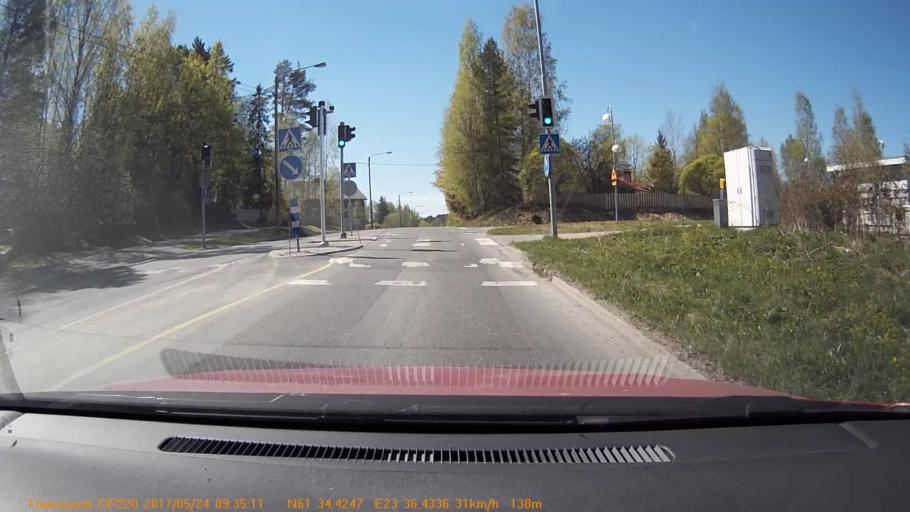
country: FI
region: Pirkanmaa
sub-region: Tampere
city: Yloejaervi
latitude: 61.5738
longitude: 23.6072
